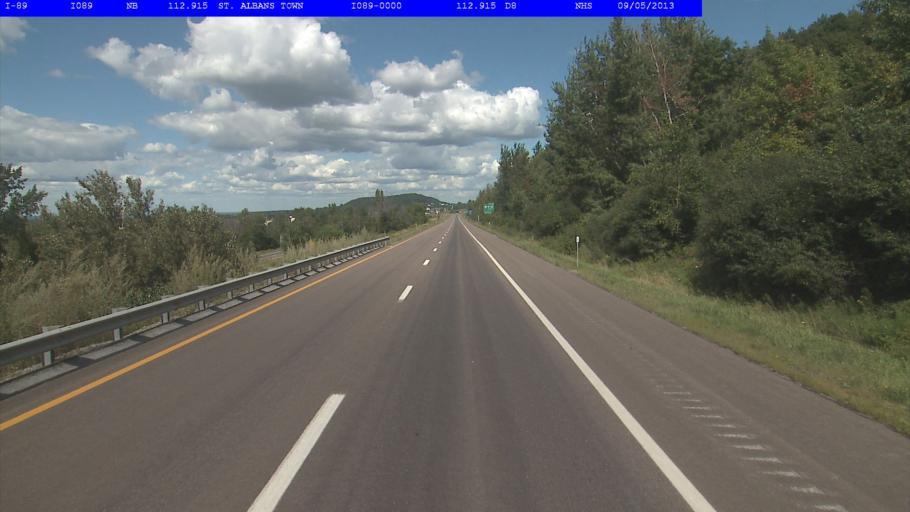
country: US
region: Vermont
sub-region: Franklin County
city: Saint Albans
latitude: 44.7831
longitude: -73.0727
